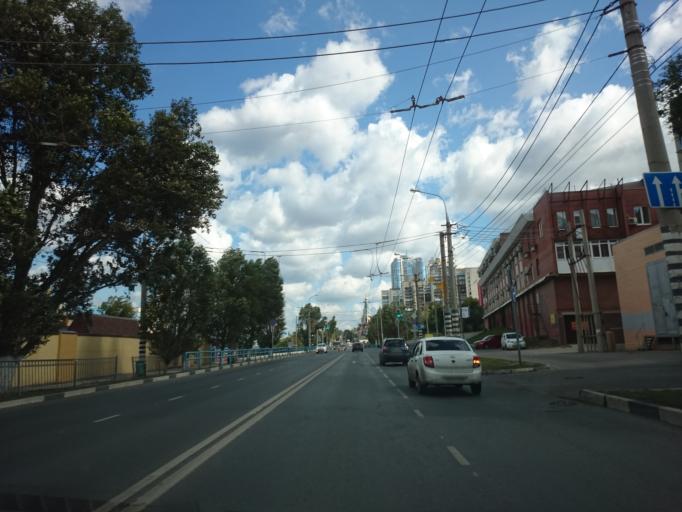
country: RU
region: Samara
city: Samara
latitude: 53.2120
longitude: 50.1259
